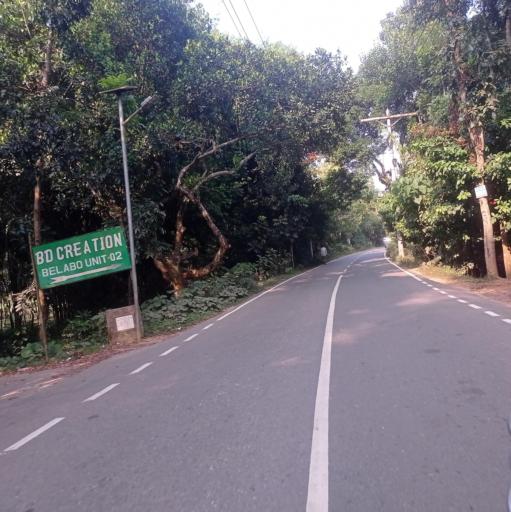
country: BD
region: Dhaka
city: Bhairab Bazar
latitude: 24.0573
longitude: 90.8374
